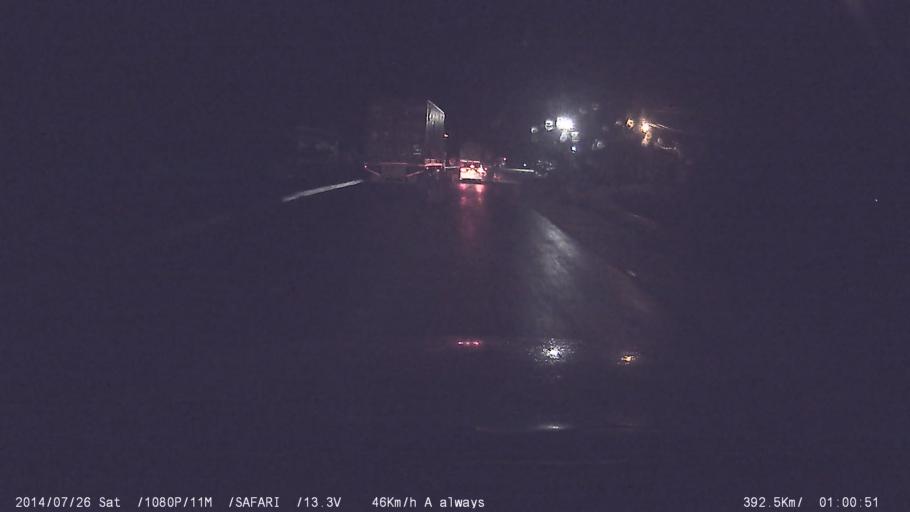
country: IN
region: Kerala
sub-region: Palakkad district
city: Palakkad
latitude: 10.7796
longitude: 76.7125
